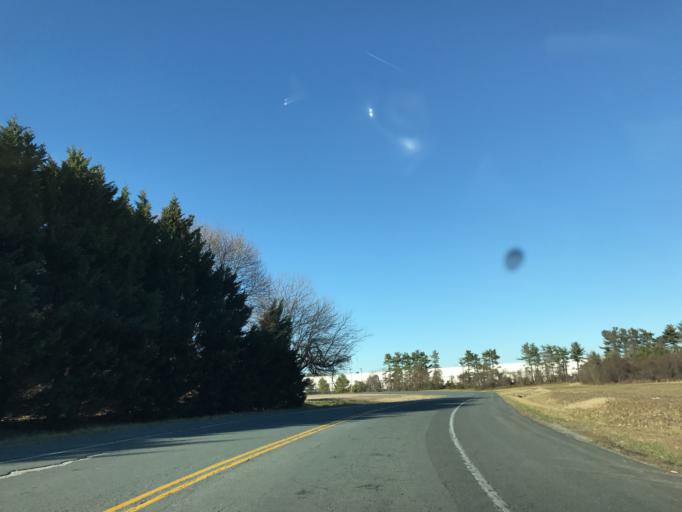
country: US
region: Maryland
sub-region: Harford County
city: Perryman
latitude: 39.4678
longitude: -76.2030
